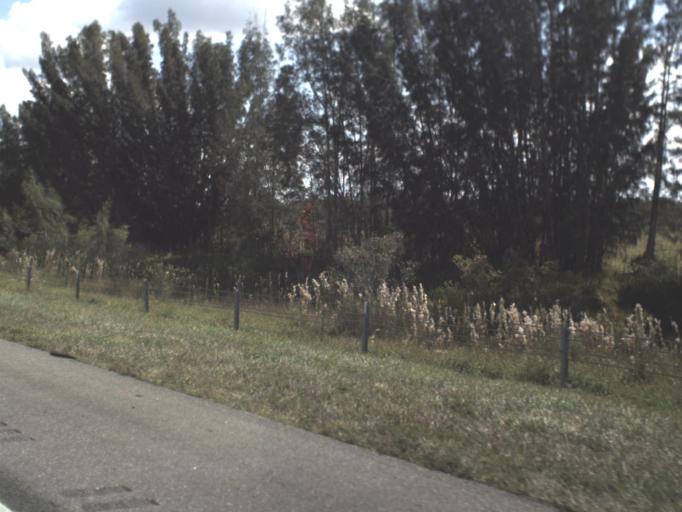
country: US
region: Florida
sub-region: Indian River County
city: Fellsmere
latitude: 27.7813
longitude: -80.9723
